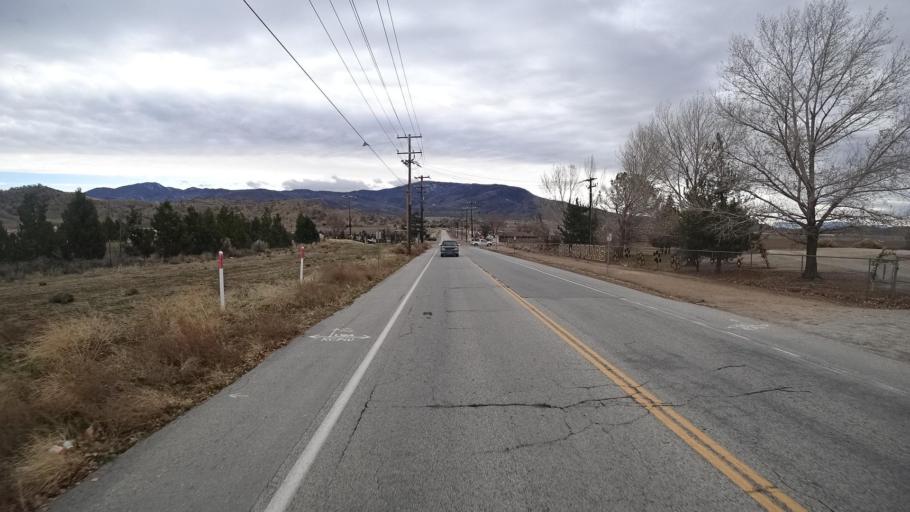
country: US
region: California
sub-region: Kern County
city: Bear Valley Springs
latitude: 35.1318
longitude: -118.5746
